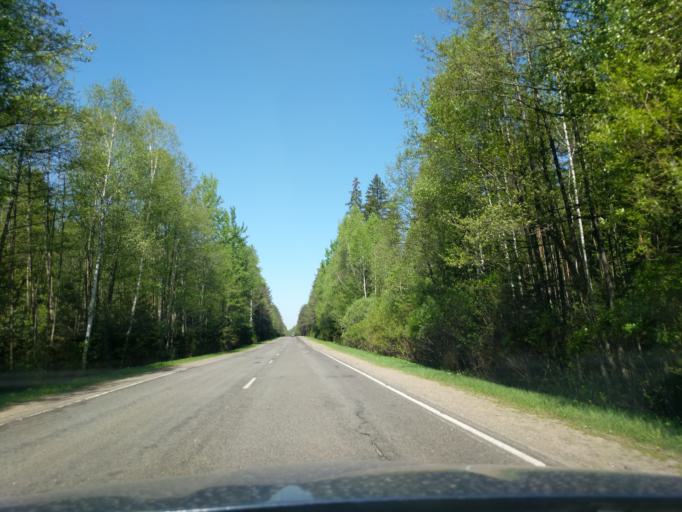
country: BY
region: Minsk
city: Il'ya
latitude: 54.4042
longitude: 27.3203
